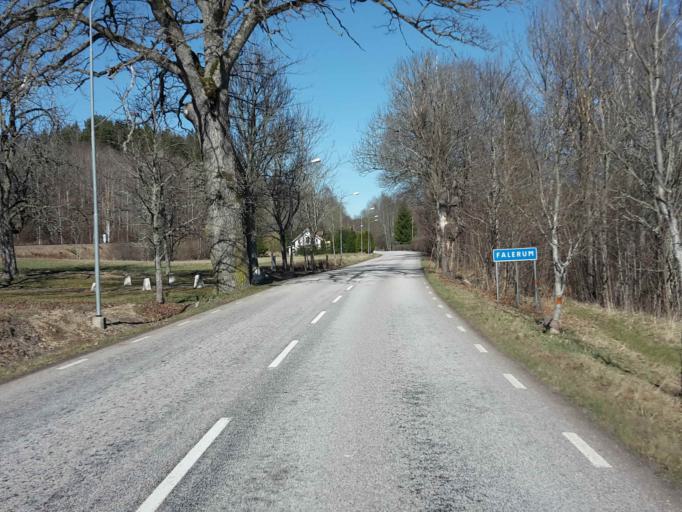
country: SE
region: Kalmar
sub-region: Vasterviks Kommun
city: Overum
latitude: 58.1378
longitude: 16.2161
